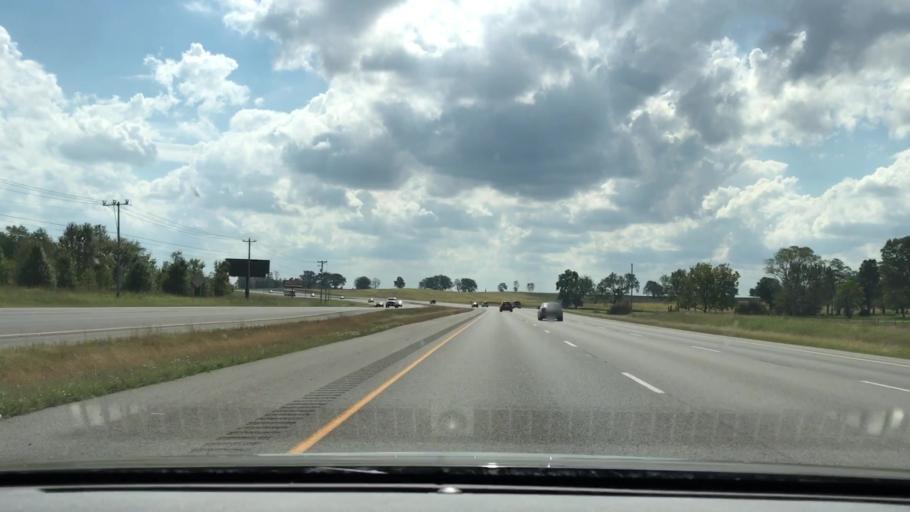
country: US
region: Kentucky
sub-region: Christian County
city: Oak Grove
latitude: 36.6921
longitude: -87.4531
